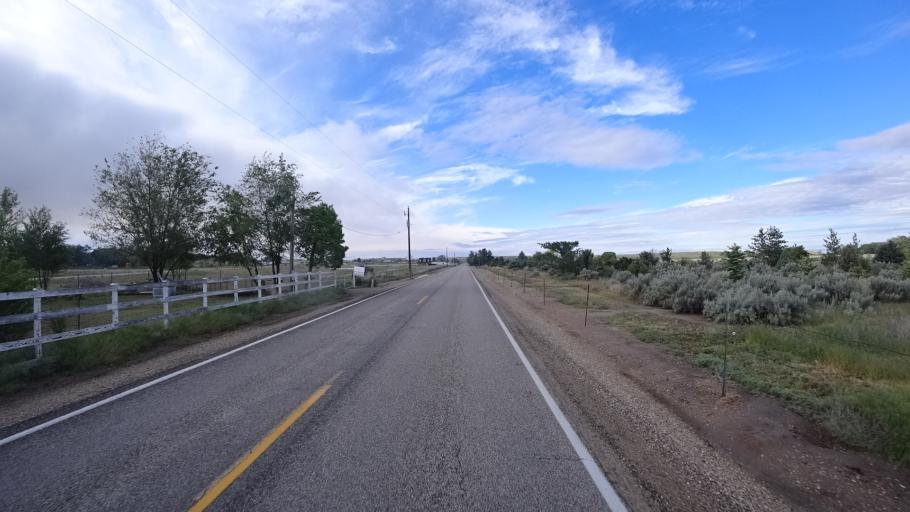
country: US
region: Idaho
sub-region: Ada County
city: Star
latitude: 43.7783
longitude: -116.4732
